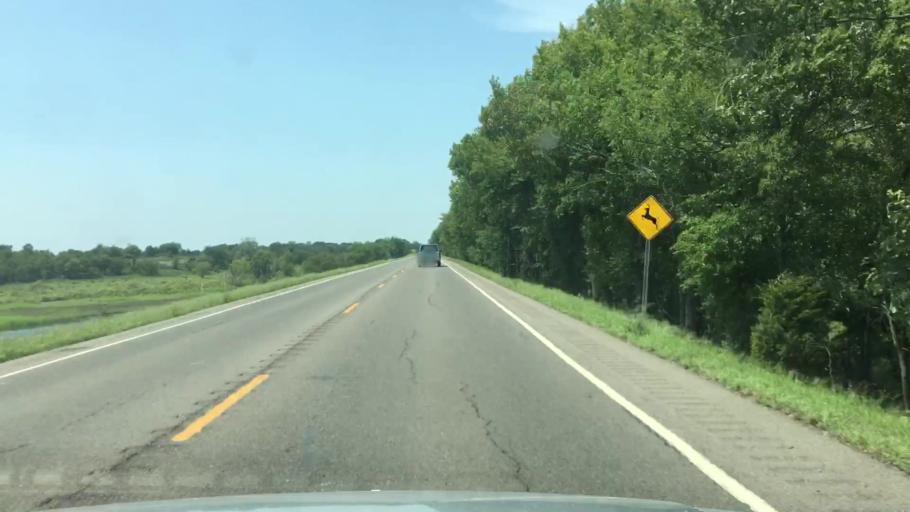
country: US
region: Oklahoma
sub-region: Wagoner County
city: Wagoner
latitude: 35.9371
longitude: -95.3276
